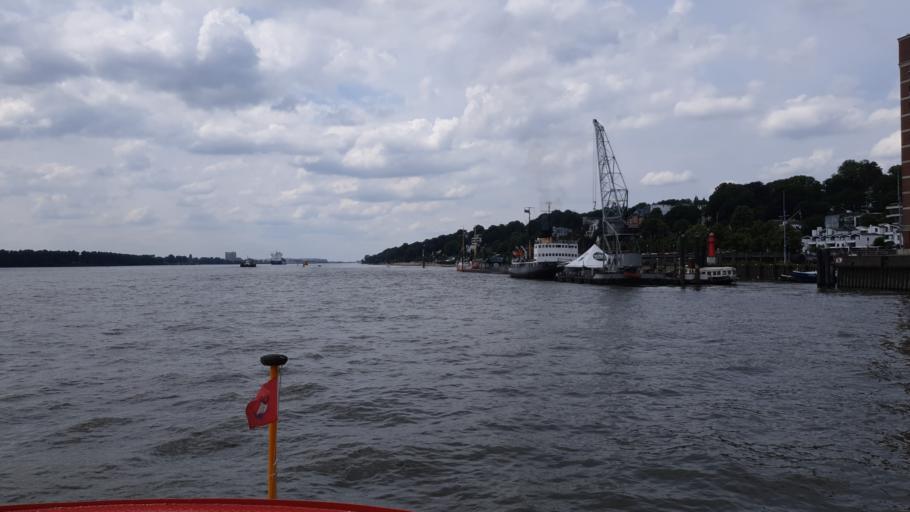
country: DE
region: Hamburg
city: Altona
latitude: 53.5428
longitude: 9.9179
